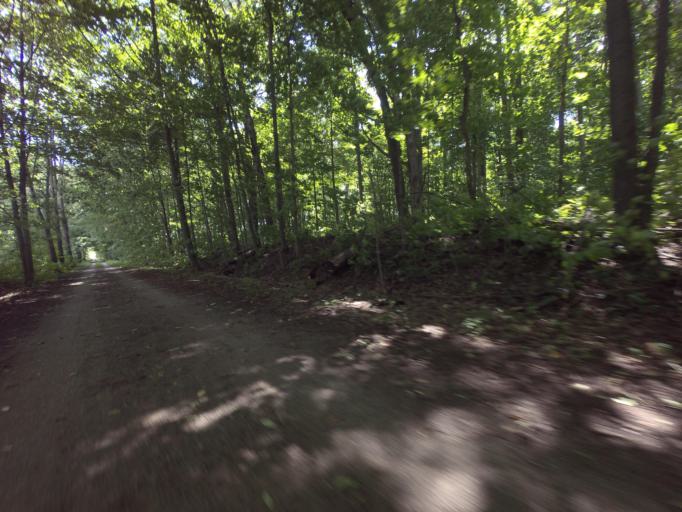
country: CA
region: Ontario
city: Orangeville
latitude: 43.7889
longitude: -80.2518
